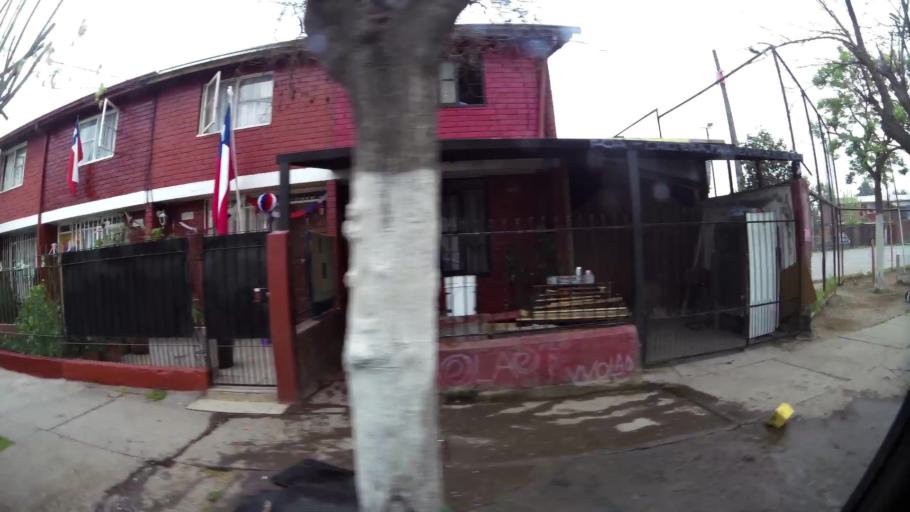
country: CL
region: Santiago Metropolitan
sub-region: Provincia de Santiago
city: Lo Prado
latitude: -33.5062
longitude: -70.7429
